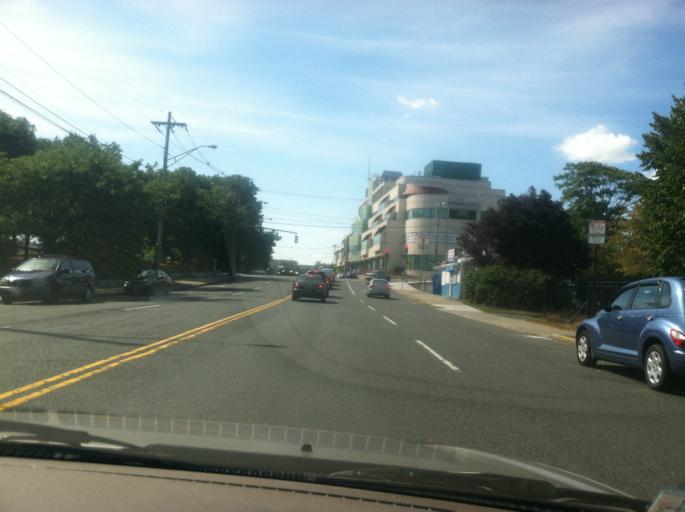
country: US
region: Massachusetts
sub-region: Suffolk County
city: Revere
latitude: 42.4091
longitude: -70.9917
